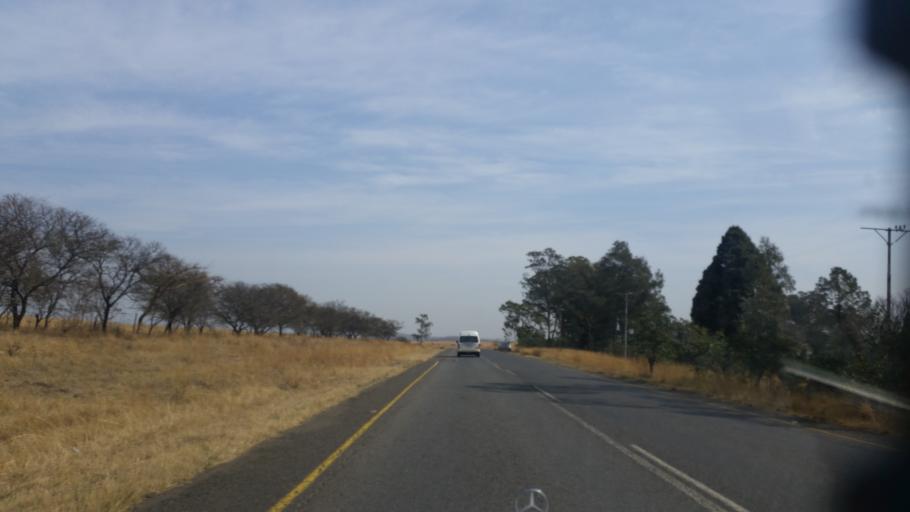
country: ZA
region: KwaZulu-Natal
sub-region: uThukela District Municipality
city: Estcourt
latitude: -29.0549
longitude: 29.9256
